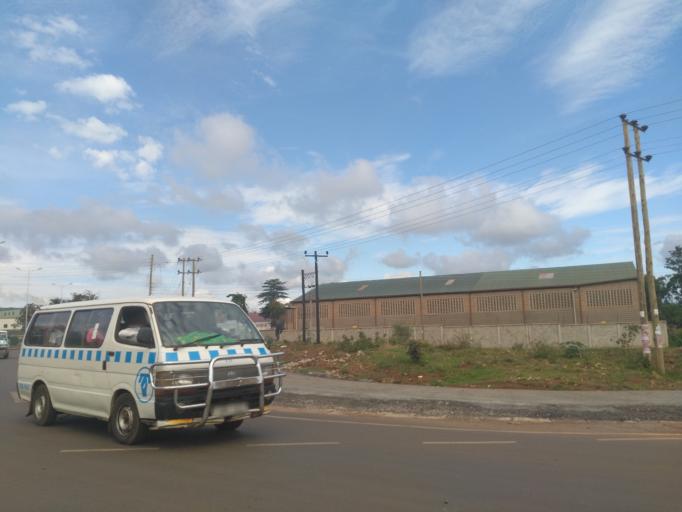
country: UG
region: Eastern Region
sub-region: Jinja District
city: Jinja
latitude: 0.4384
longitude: 33.1838
